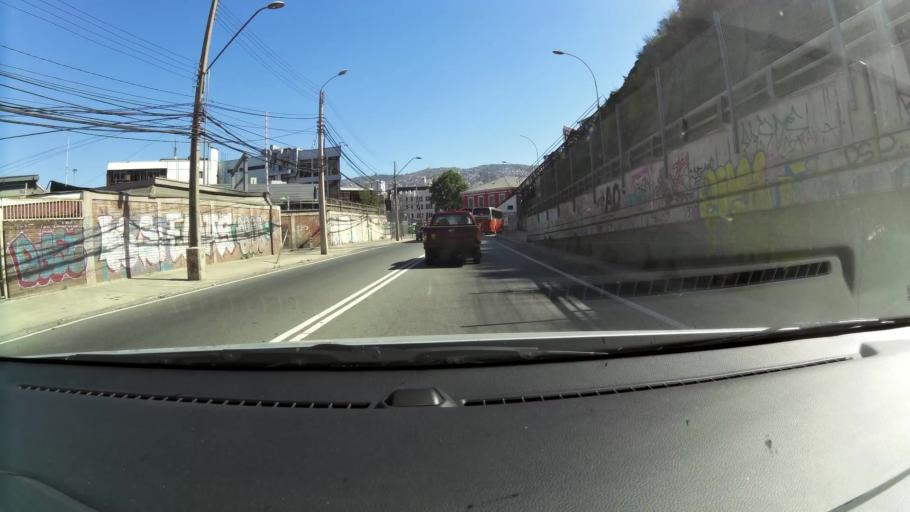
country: CL
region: Valparaiso
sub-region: Provincia de Valparaiso
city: Valparaiso
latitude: -33.0329
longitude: -71.6298
